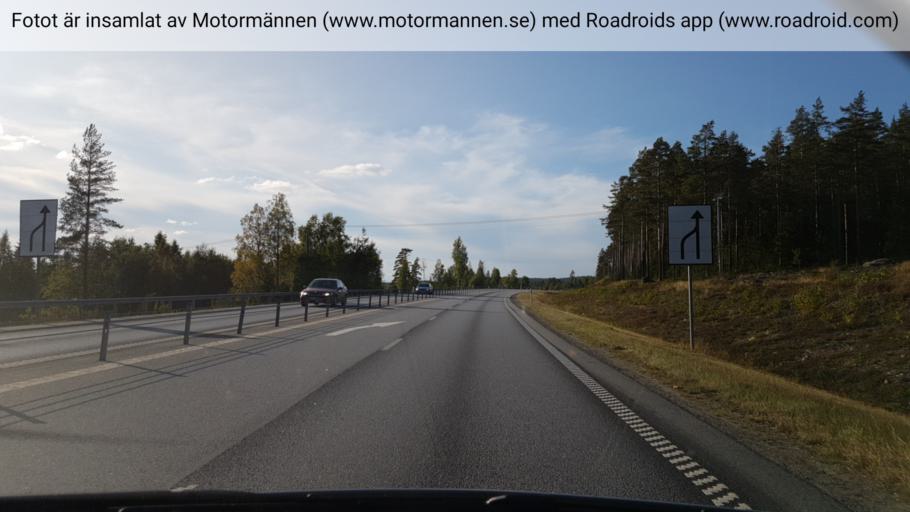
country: SE
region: Vaesterbotten
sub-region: Vannas Kommun
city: Vannasby
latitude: 63.8882
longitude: 20.0022
